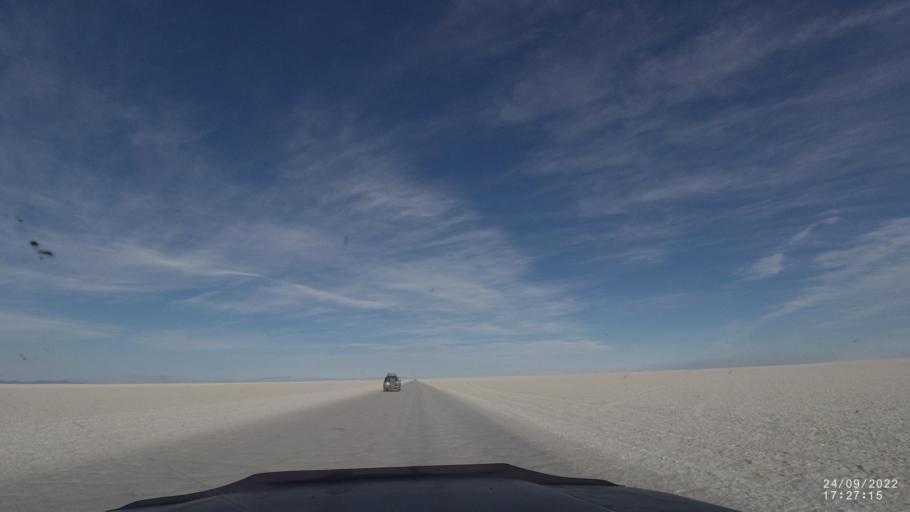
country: BO
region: Potosi
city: Colchani
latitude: -20.2991
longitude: -67.4525
